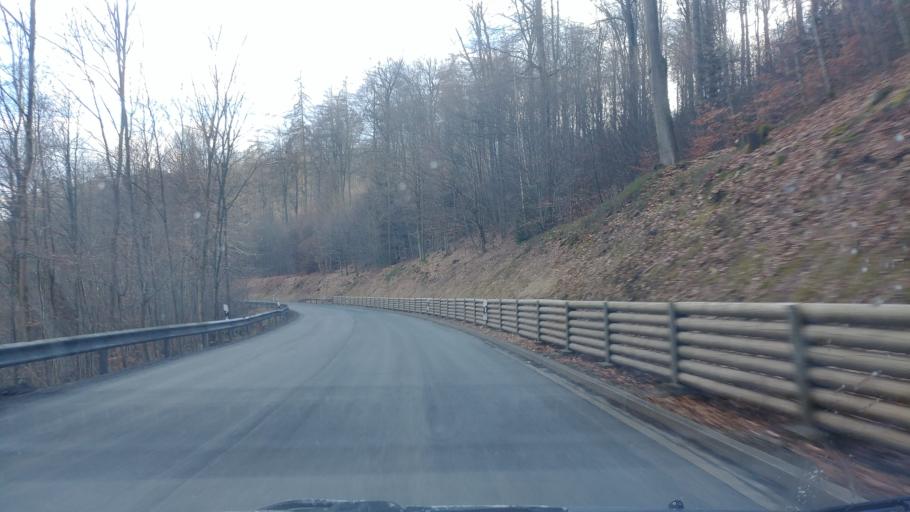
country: DE
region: Lower Saxony
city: Holzminden
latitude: 51.7843
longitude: 9.4775
